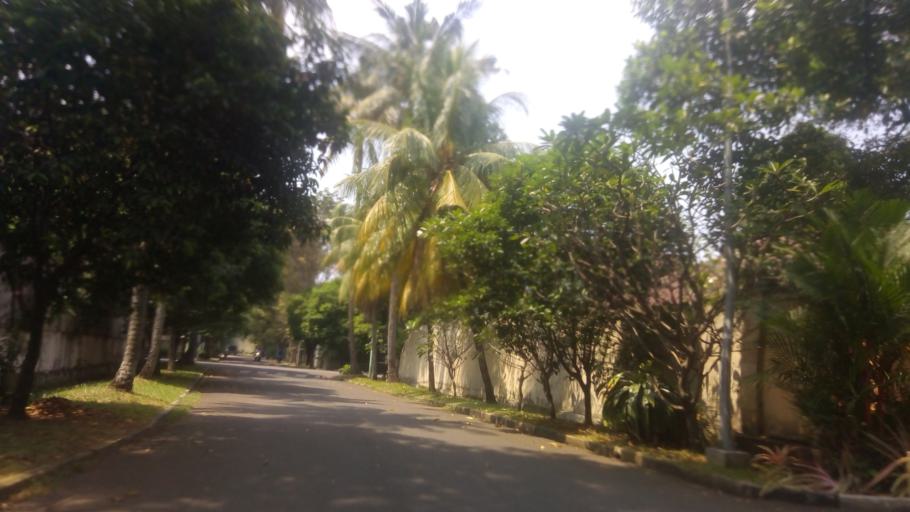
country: ID
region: Jakarta Raya
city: Jakarta
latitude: -6.2366
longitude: 106.8339
